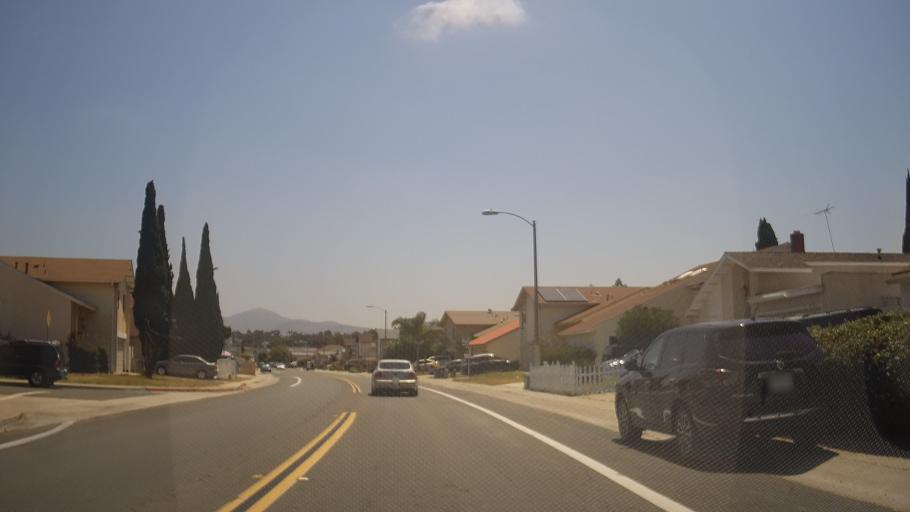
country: US
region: California
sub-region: San Diego County
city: Bonita
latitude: 32.6657
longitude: -117.0551
